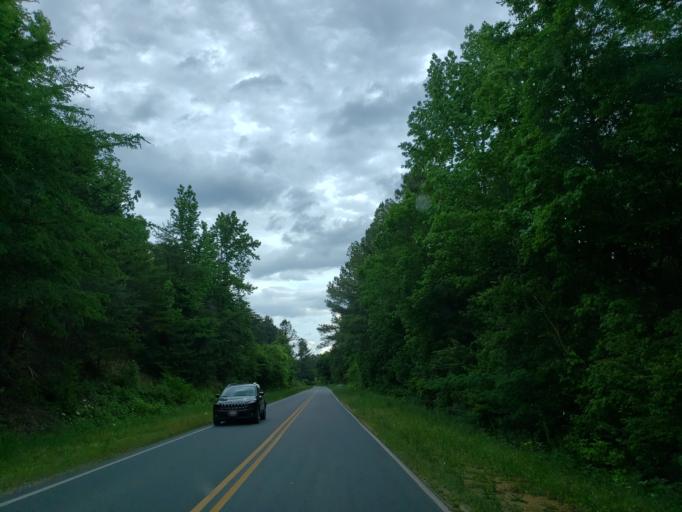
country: US
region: Georgia
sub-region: Polk County
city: Rockmart
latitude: 33.9663
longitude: -85.0487
